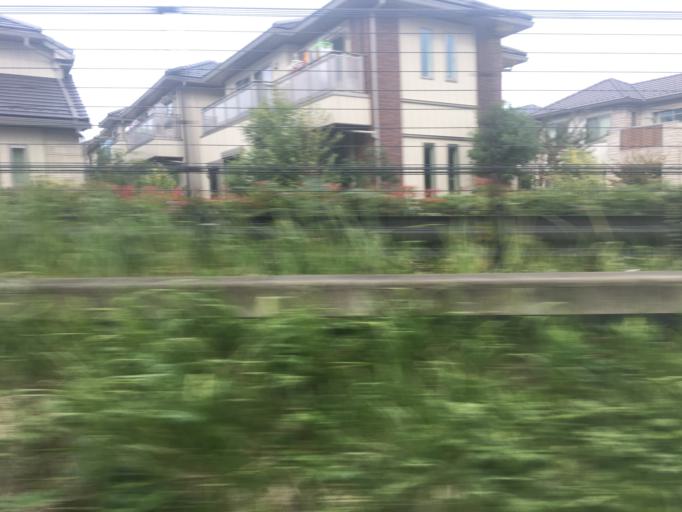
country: JP
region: Saitama
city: Kawagoe
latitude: 35.9088
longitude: 139.4786
